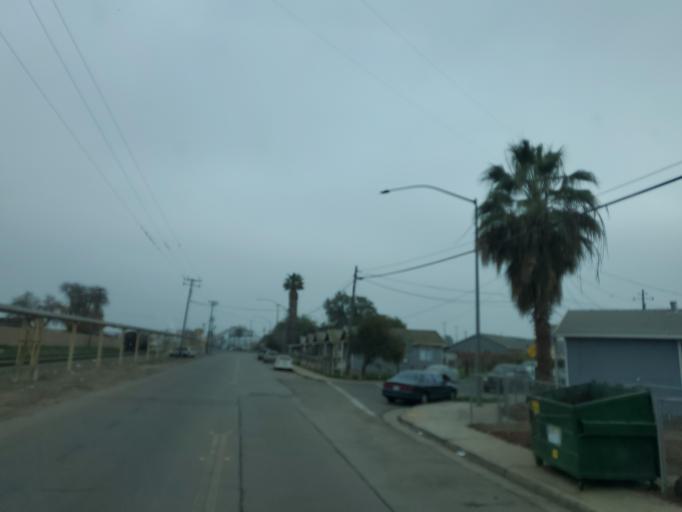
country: US
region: California
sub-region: San Joaquin County
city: Stockton
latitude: 37.9485
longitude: -121.3148
